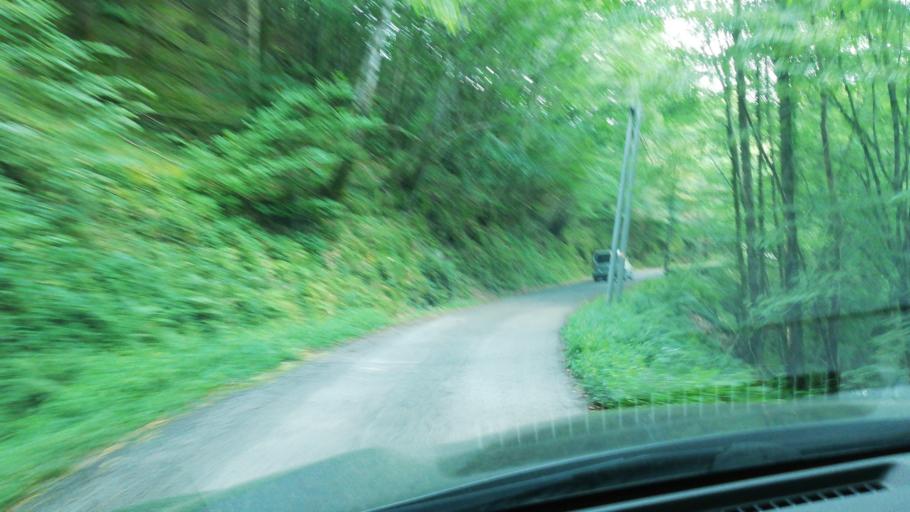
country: FR
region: Limousin
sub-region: Departement de la Correze
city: Argentat
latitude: 44.9781
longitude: 2.0290
